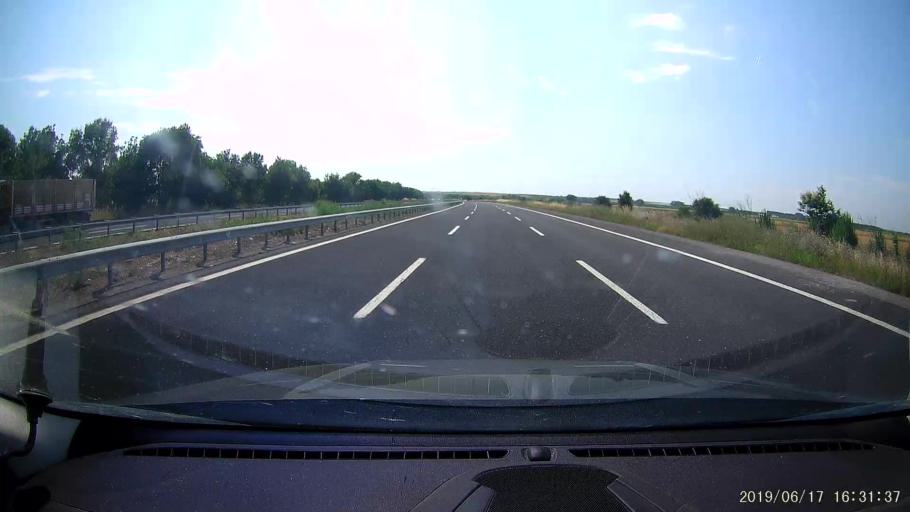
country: TR
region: Tekirdag
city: Beyazkoy
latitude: 41.3630
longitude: 27.6228
